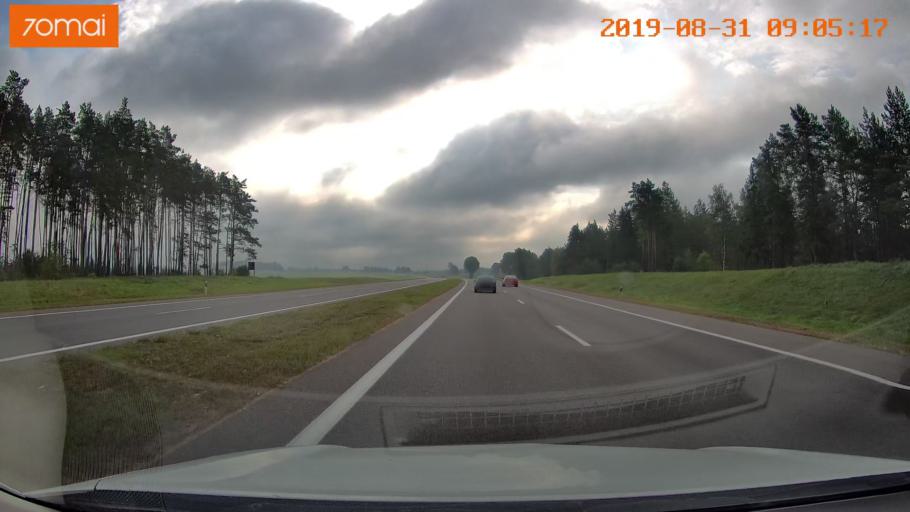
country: BY
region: Minsk
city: Chervyen'
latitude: 53.7264
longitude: 28.3709
